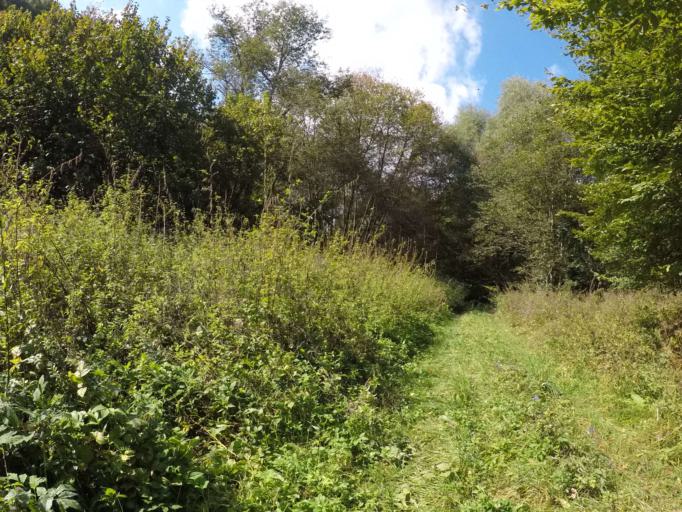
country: SK
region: Presovsky
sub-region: Okres Presov
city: Presov
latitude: 48.9360
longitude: 21.1557
